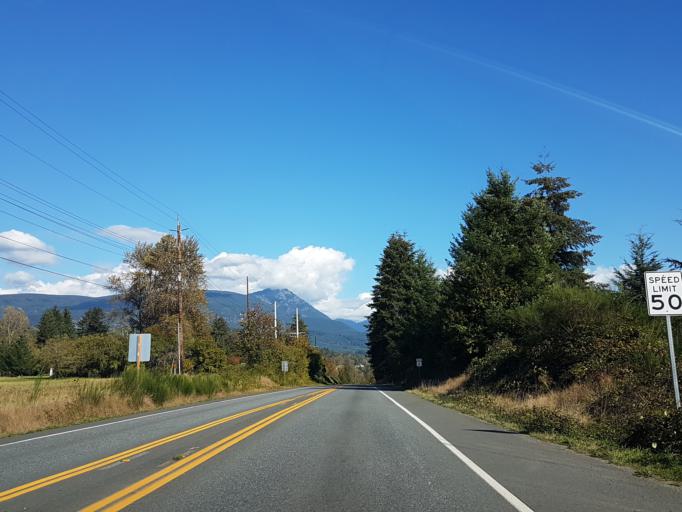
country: US
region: Washington
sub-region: Snohomish County
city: Sultan
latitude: 47.8683
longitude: -121.7747
